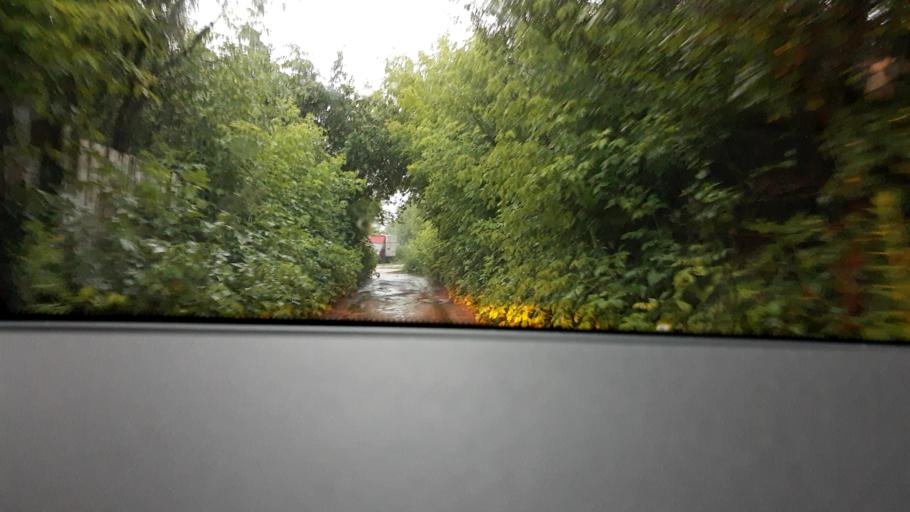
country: RU
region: Nizjnij Novgorod
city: Gorbatovka
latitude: 56.2601
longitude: 43.8272
